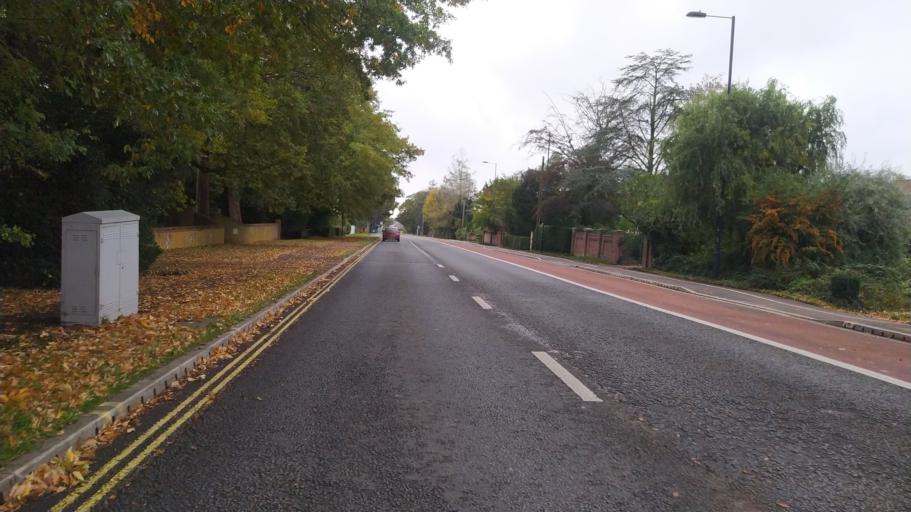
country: GB
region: England
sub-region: Hampshire
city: Cowplain
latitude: 50.9056
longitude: -1.0106
